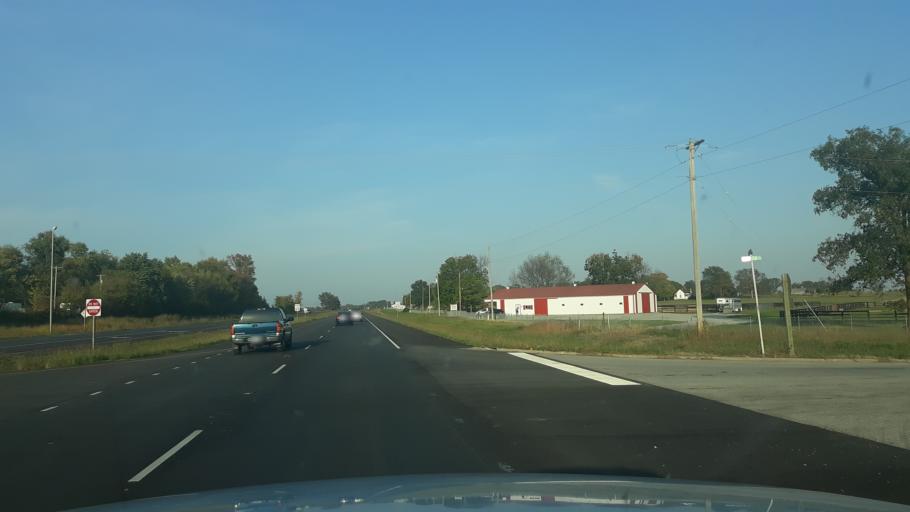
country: US
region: Illinois
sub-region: Saline County
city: Eldorado
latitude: 37.7868
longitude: -88.4856
